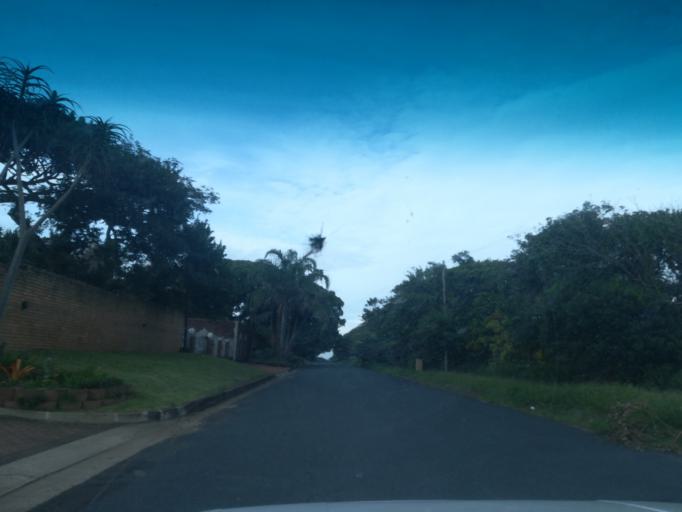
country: ZA
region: KwaZulu-Natal
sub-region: Ugu District Municipality
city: Scottburgh
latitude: -30.2867
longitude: 30.7495
